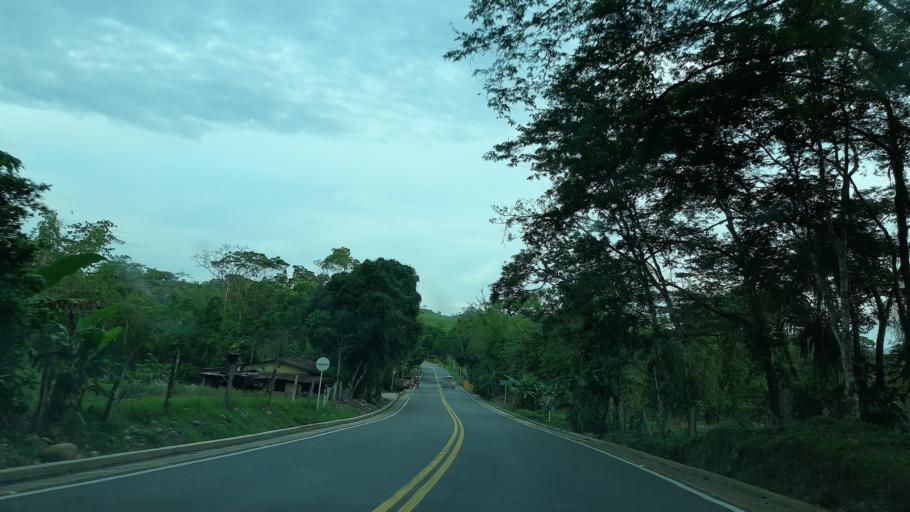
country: CO
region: Casanare
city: Sabanalarga
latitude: 4.7974
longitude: -73.0591
